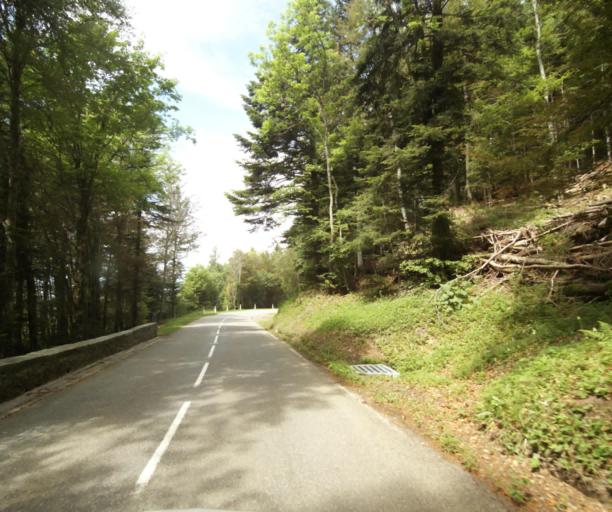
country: FR
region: Rhone-Alpes
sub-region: Departement de la Haute-Savoie
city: Perrignier
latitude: 46.2762
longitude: 6.4550
